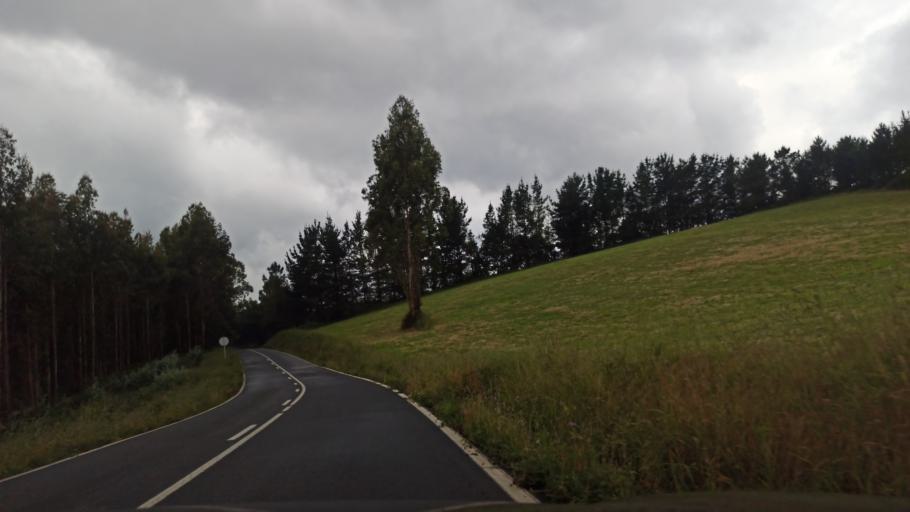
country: ES
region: Galicia
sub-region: Provincia da Coruna
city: Santiso
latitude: 42.7842
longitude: -8.0733
